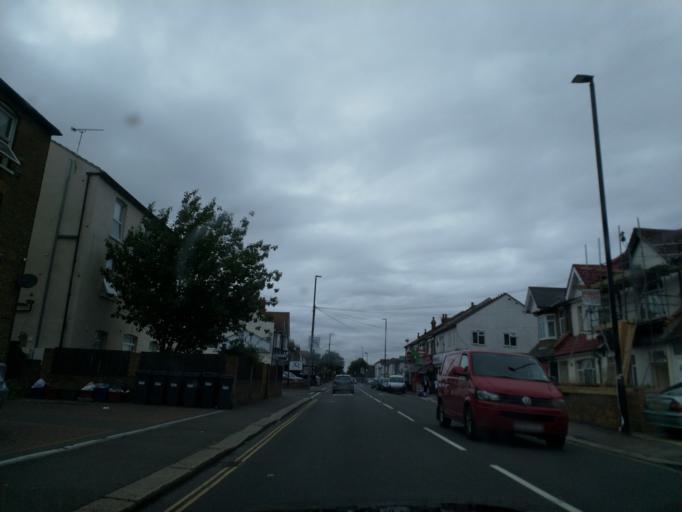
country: GB
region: England
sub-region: Greater London
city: Hounslow
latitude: 51.4607
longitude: -0.3751
